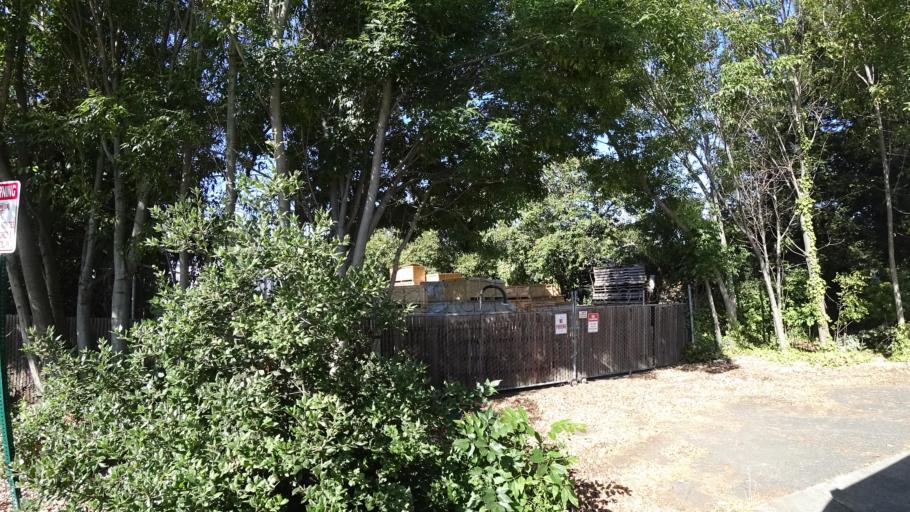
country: US
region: California
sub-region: Alameda County
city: Union City
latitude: 37.6147
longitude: -122.0474
